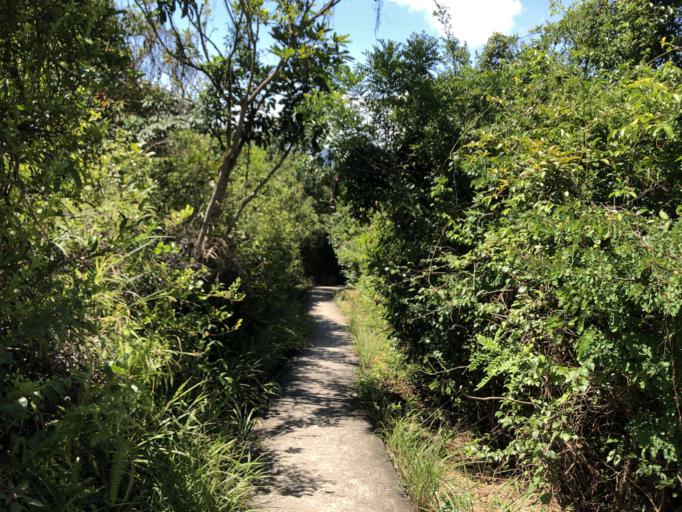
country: HK
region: Tuen Mun
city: Tuen Mun
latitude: 22.2870
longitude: 113.9817
